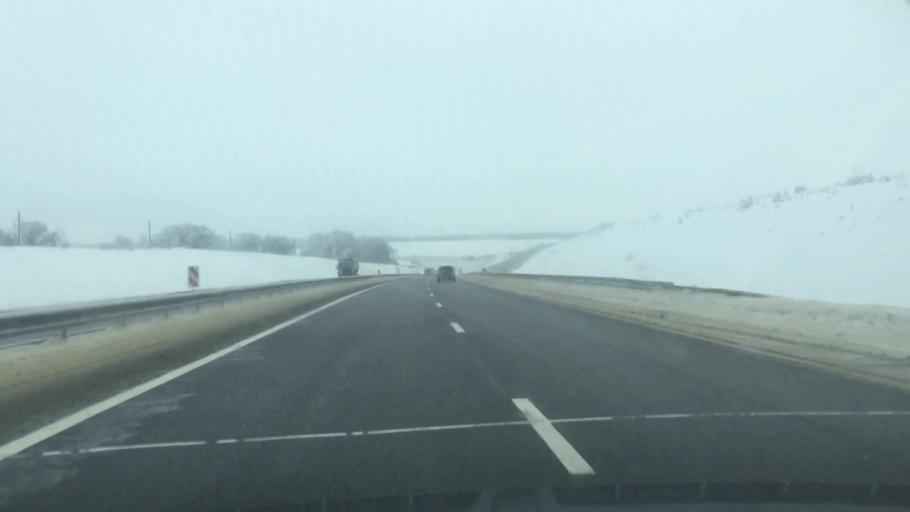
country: RU
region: Lipetsk
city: Stanovoye
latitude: 52.8733
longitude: 38.2779
